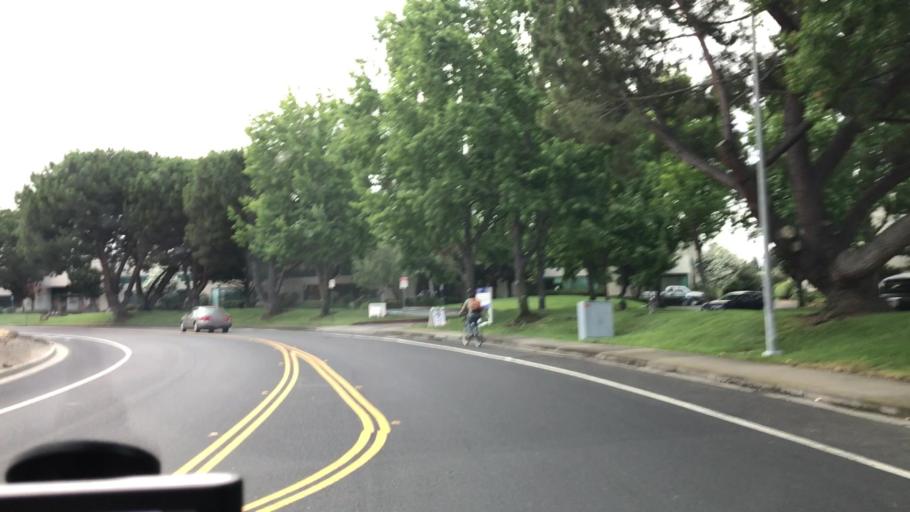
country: US
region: California
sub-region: Alameda County
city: Livermore
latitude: 37.6953
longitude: -121.7415
